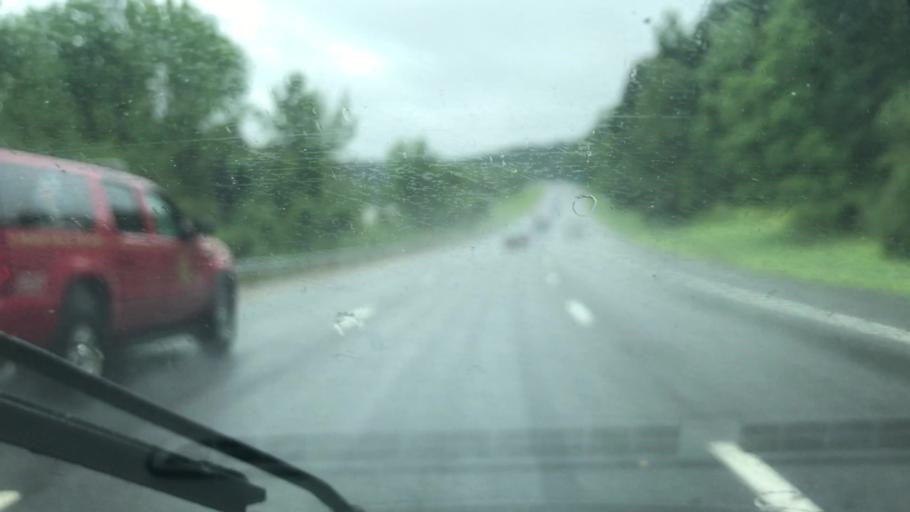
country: US
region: New York
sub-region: Westchester County
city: Yorktown Heights
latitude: 41.2471
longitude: -73.8131
